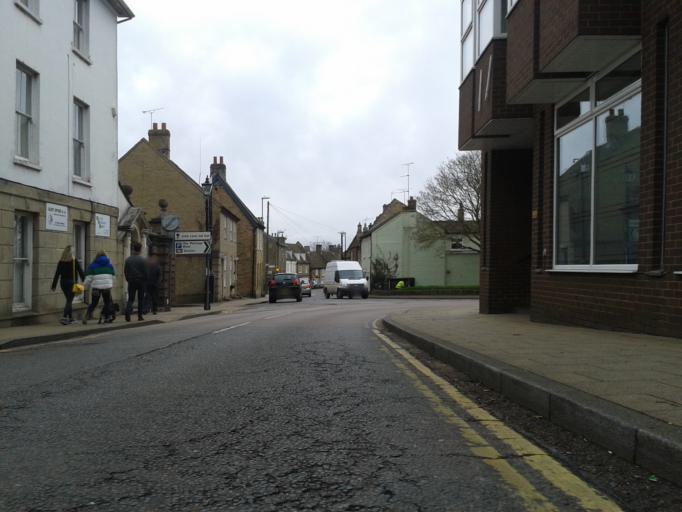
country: GB
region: England
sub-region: Cambridgeshire
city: Ely
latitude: 52.3980
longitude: 0.2682
